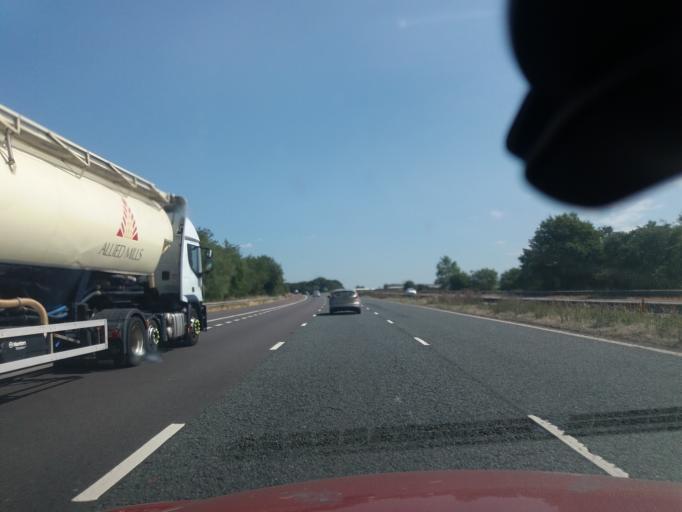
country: GB
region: England
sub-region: Borough of Bolton
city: Blackrod
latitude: 53.5962
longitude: -2.5706
